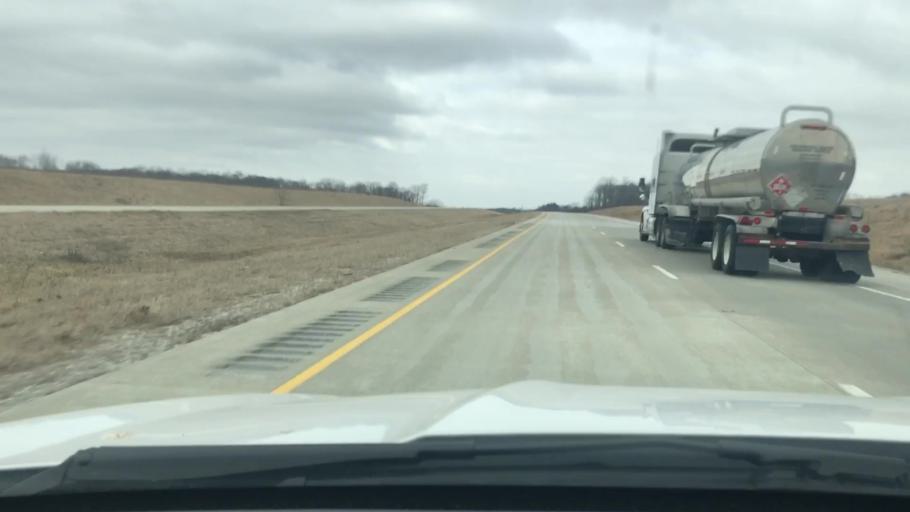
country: US
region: Indiana
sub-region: Carroll County
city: Delphi
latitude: 40.5831
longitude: -86.6495
